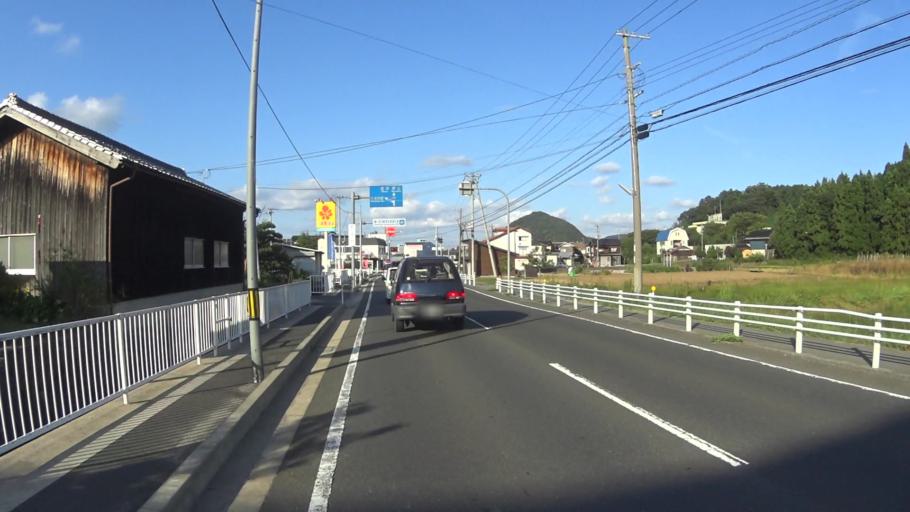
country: JP
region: Hyogo
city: Toyooka
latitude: 35.6004
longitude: 134.8920
